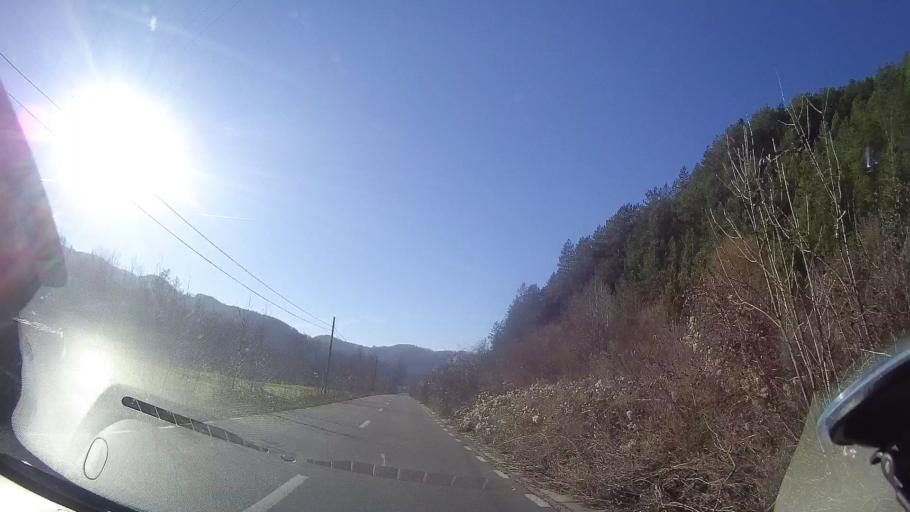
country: RO
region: Bihor
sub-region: Comuna Bratca
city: Bratca
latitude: 46.9267
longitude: 22.6305
